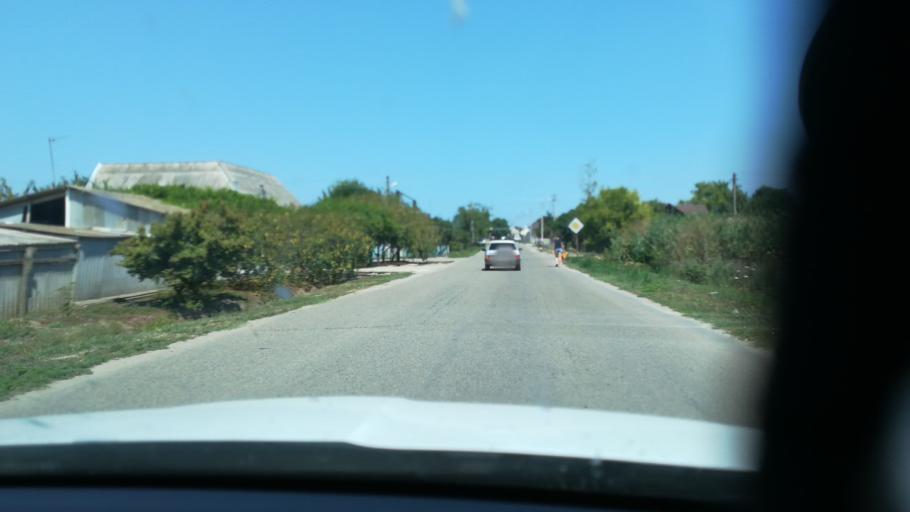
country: RU
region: Krasnodarskiy
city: Starotitarovskaya
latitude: 45.2112
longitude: 37.1447
